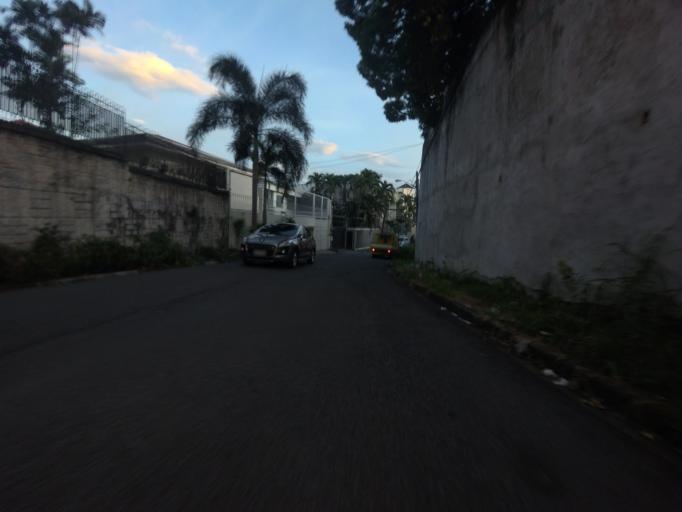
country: PH
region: Metro Manila
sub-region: San Juan
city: San Juan
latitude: 14.5952
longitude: 121.0345
